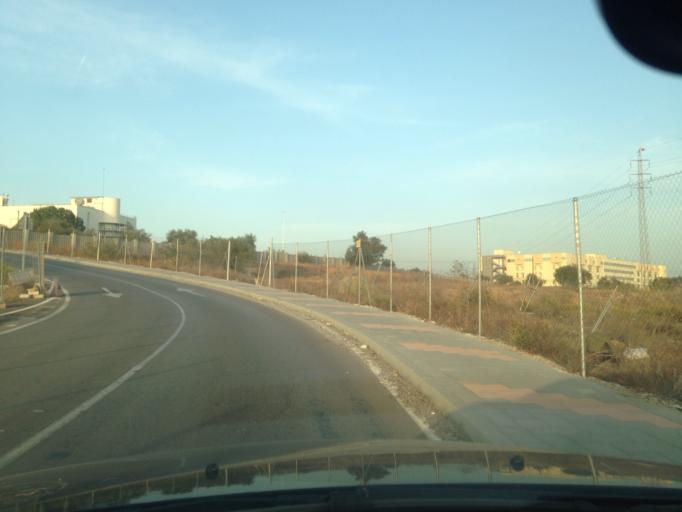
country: ES
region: Andalusia
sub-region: Provincia de Malaga
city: Malaga
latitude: 36.7173
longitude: -4.4825
